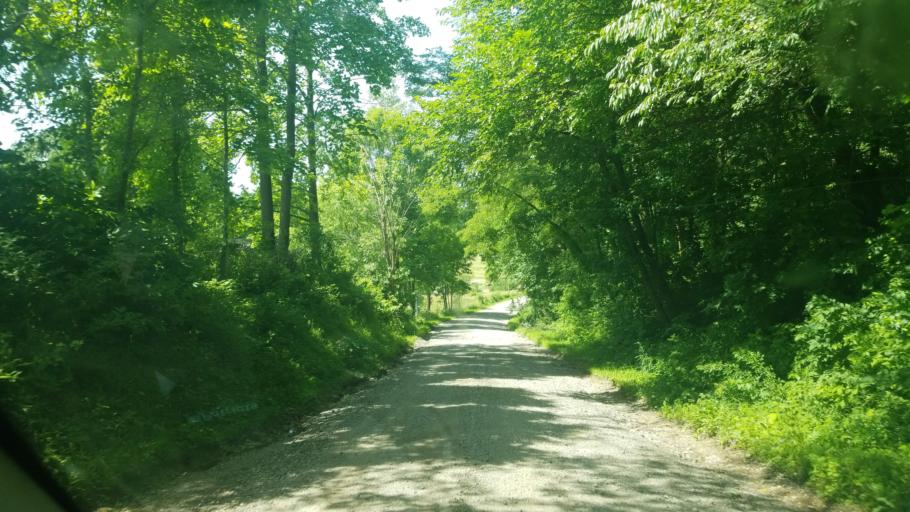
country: US
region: Ohio
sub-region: Stark County
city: Beach City
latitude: 40.6486
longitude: -81.6257
